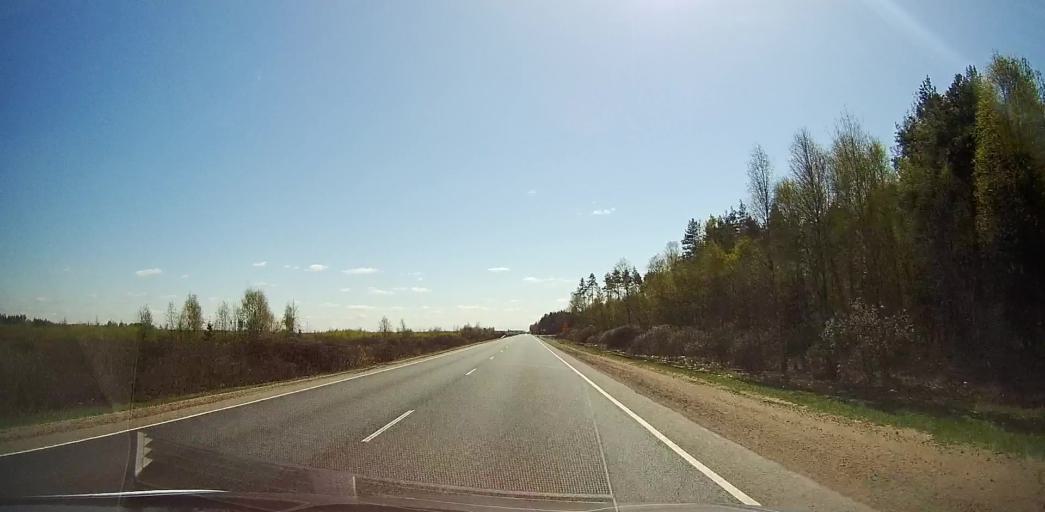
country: RU
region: Moskovskaya
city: Gzhel'
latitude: 55.5985
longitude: 38.3793
